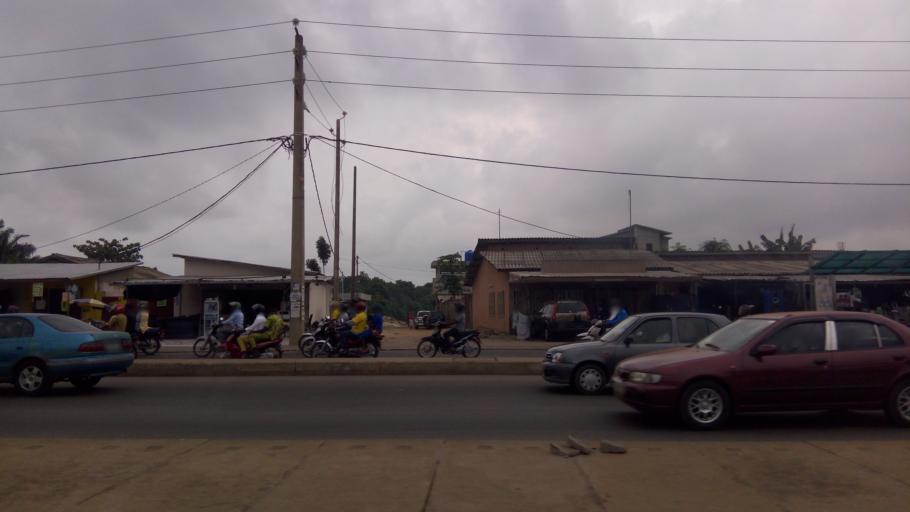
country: BJ
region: Littoral
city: Cotonou
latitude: 6.3886
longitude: 2.3636
